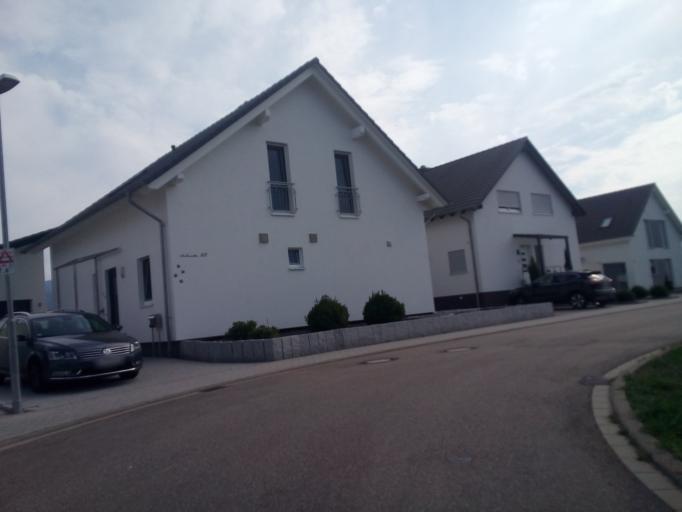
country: DE
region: Baden-Wuerttemberg
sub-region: Freiburg Region
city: Sasbach
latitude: 48.6562
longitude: 8.0859
